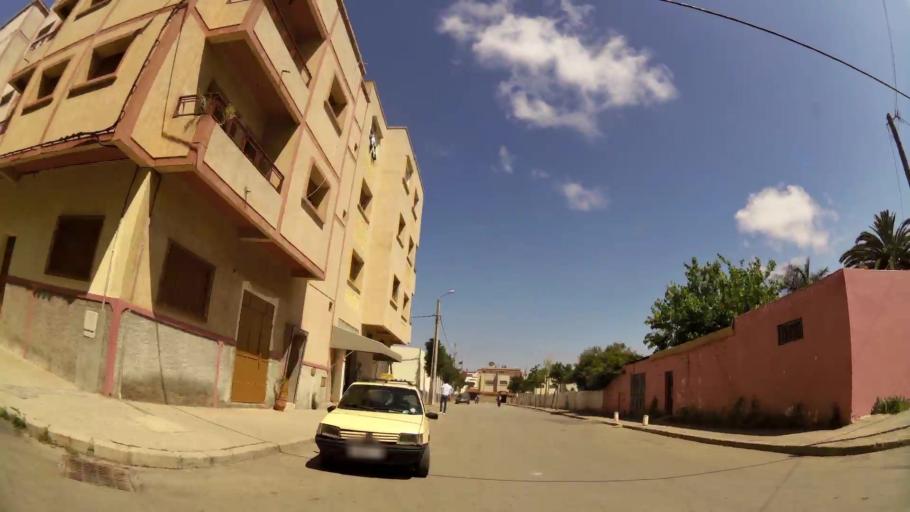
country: MA
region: Rabat-Sale-Zemmour-Zaer
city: Sale
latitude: 34.0443
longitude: -6.7887
